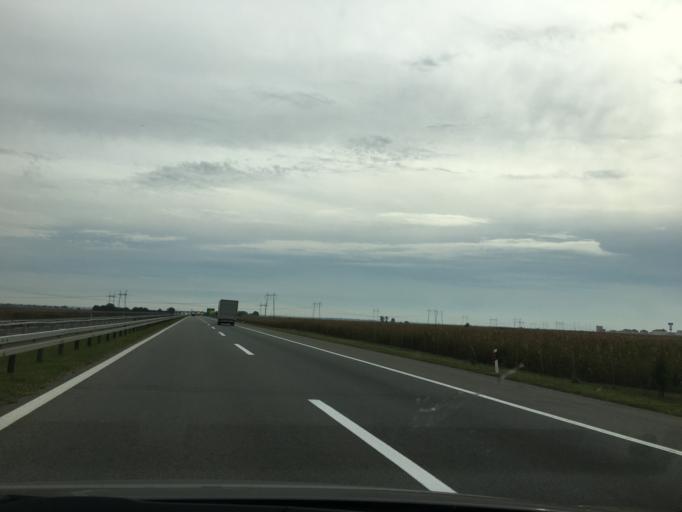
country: RS
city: Novi Karlovci
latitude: 45.0820
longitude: 20.1363
